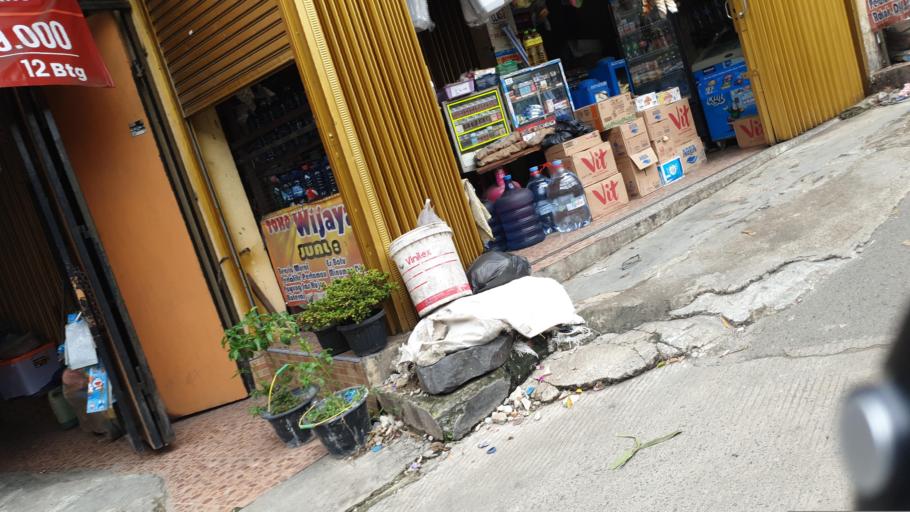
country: ID
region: Jakarta Raya
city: Jakarta
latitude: -6.2482
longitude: 106.7863
